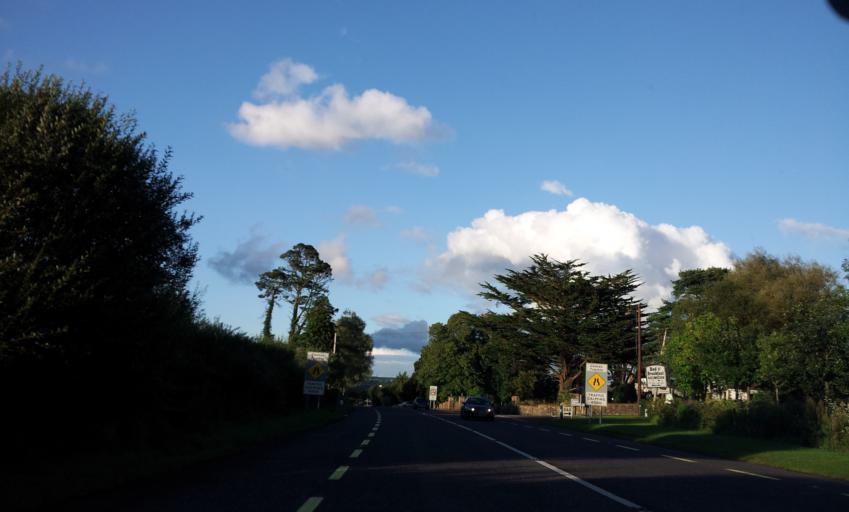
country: IE
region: Munster
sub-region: County Limerick
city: Abbeyfeale
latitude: 52.3720
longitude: -9.3135
